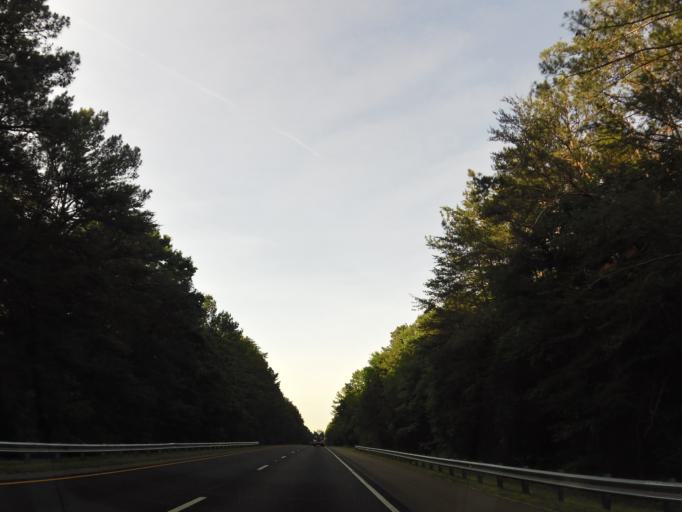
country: US
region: Alabama
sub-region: DeKalb County
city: Fort Payne
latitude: 34.4031
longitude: -85.7807
